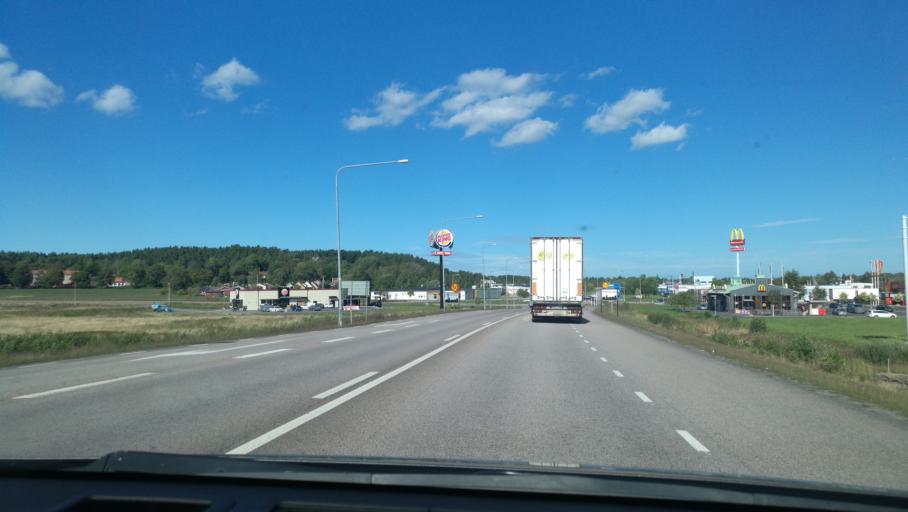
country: SE
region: Vaestra Goetaland
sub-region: Mariestads Kommun
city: Mariestad
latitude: 58.6765
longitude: 13.8165
